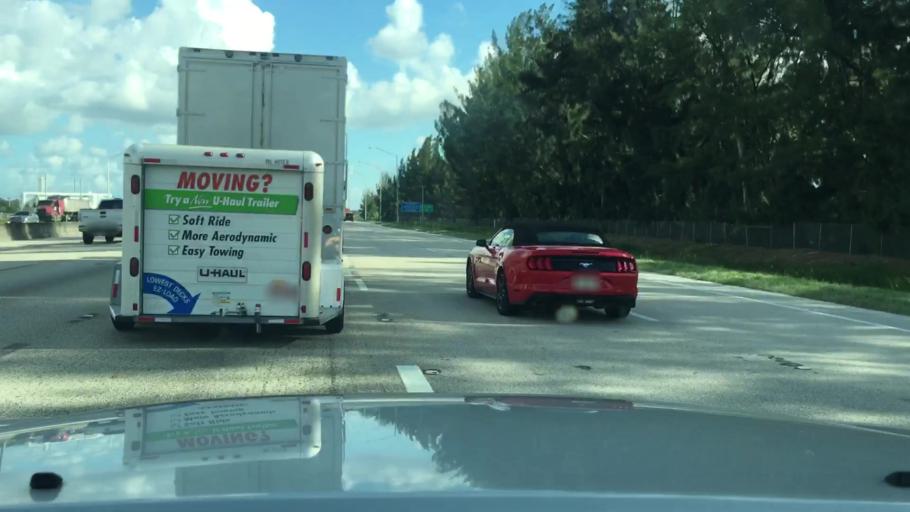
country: US
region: Florida
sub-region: Miami-Dade County
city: Doral
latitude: 25.8022
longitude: -80.3836
